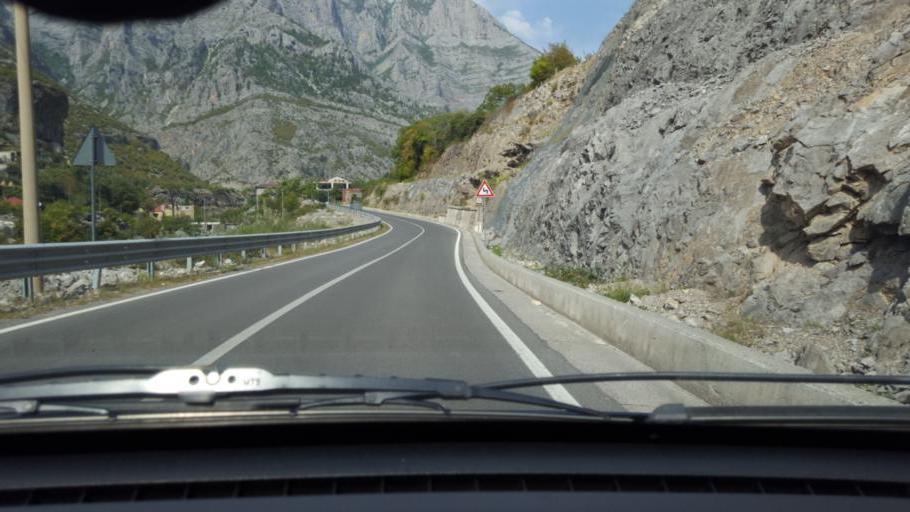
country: AL
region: Shkoder
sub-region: Rrethi i Malesia e Madhe
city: Kastrat
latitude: 42.4596
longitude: 19.5610
